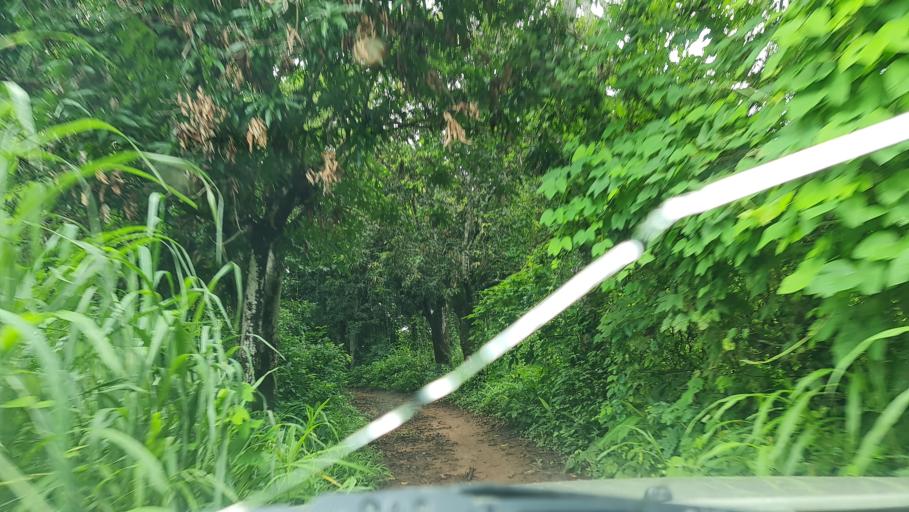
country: MW
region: Southern Region
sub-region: Nsanje District
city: Nsanje
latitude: -17.3867
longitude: 35.7791
